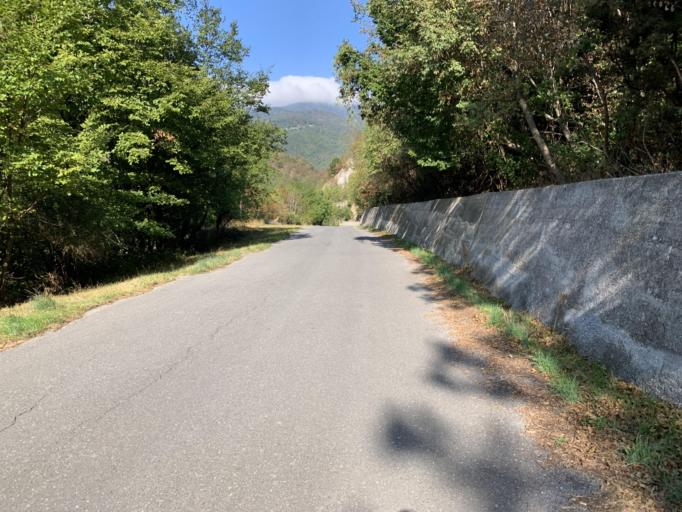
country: IT
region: Liguria
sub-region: Provincia di Savona
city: Magliolo
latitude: 44.1917
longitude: 8.2574
